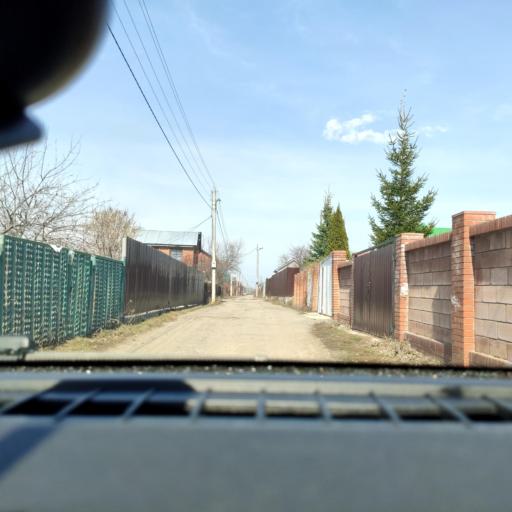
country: RU
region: Samara
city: Podstepki
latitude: 53.5109
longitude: 49.1059
